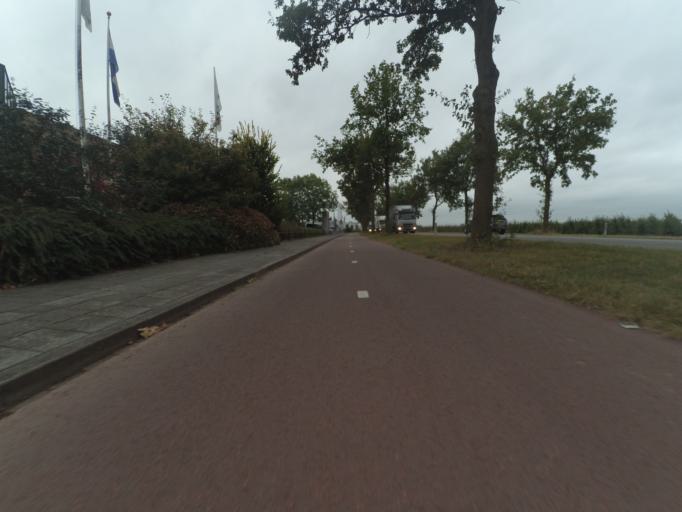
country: NL
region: Gelderland
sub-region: Gemeente Tiel
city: Tiel
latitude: 51.9134
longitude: 5.4255
